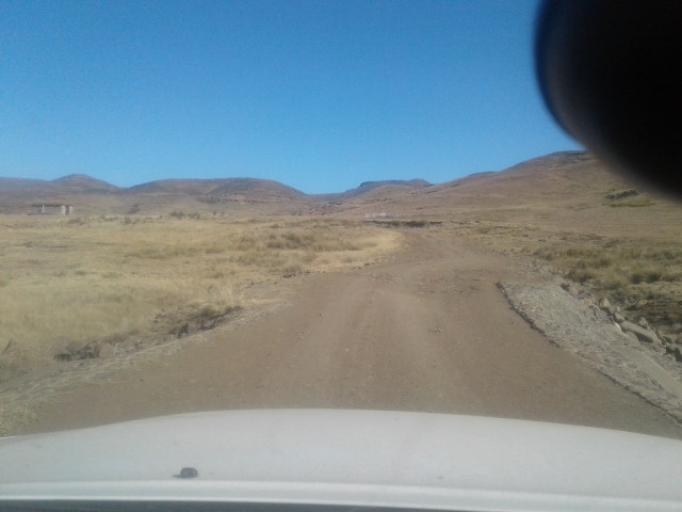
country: LS
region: Berea
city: Teyateyaneng
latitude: -29.3706
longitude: 28.0243
